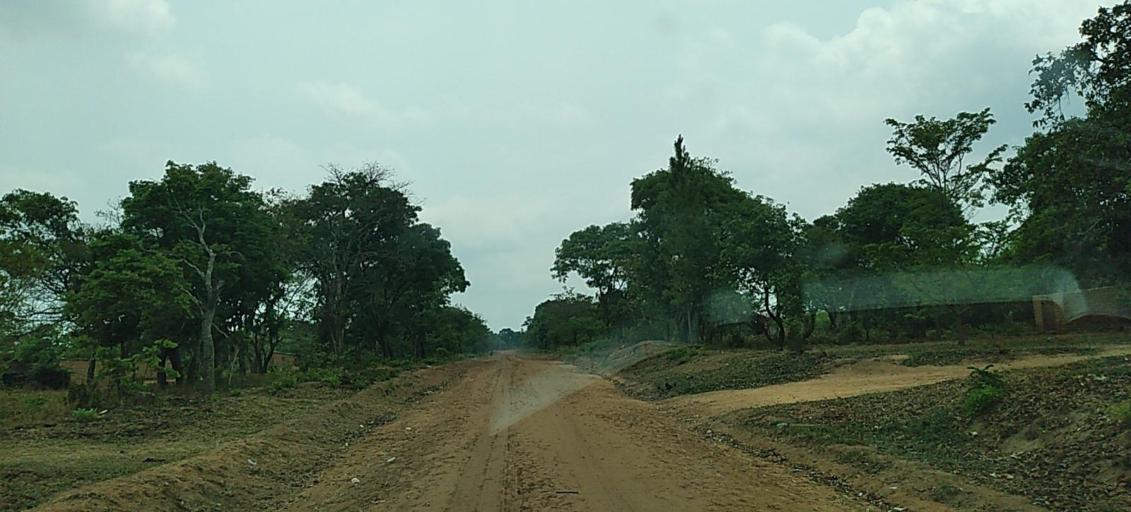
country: ZM
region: North-Western
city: Mwinilunga
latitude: -11.4504
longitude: 24.7520
